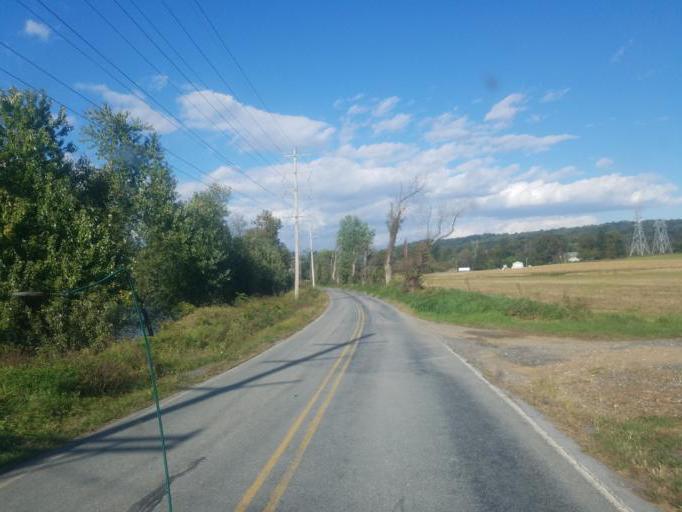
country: US
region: Pennsylvania
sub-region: Dauphin County
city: Middletown
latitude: 40.2020
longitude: -76.7141
